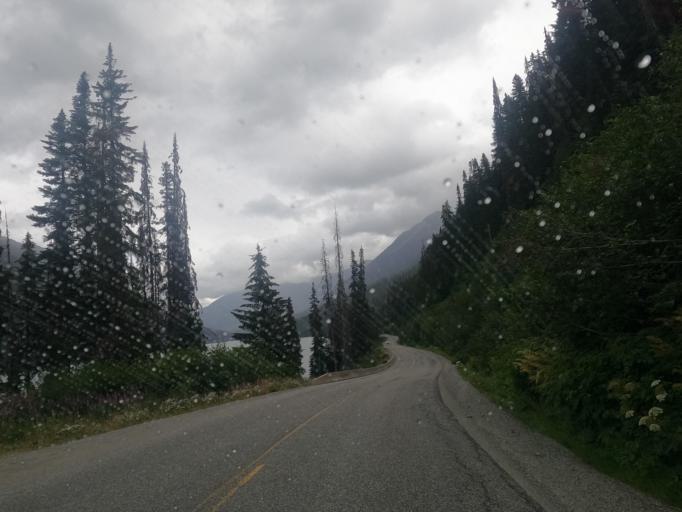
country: CA
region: British Columbia
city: Lillooet
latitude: 50.3956
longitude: -122.3267
